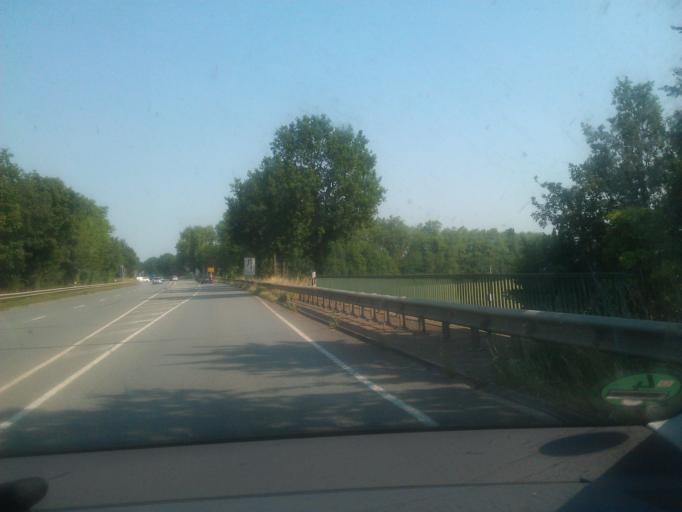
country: DE
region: North Rhine-Westphalia
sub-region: Regierungsbezirk Detmold
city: Bad Salzuflen
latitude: 52.0496
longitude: 8.7838
